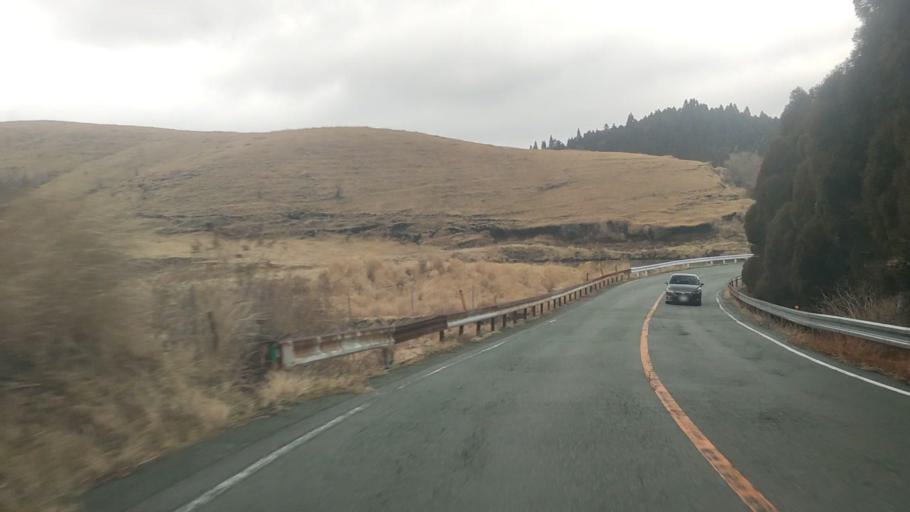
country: JP
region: Kumamoto
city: Aso
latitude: 32.8853
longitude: 131.1700
